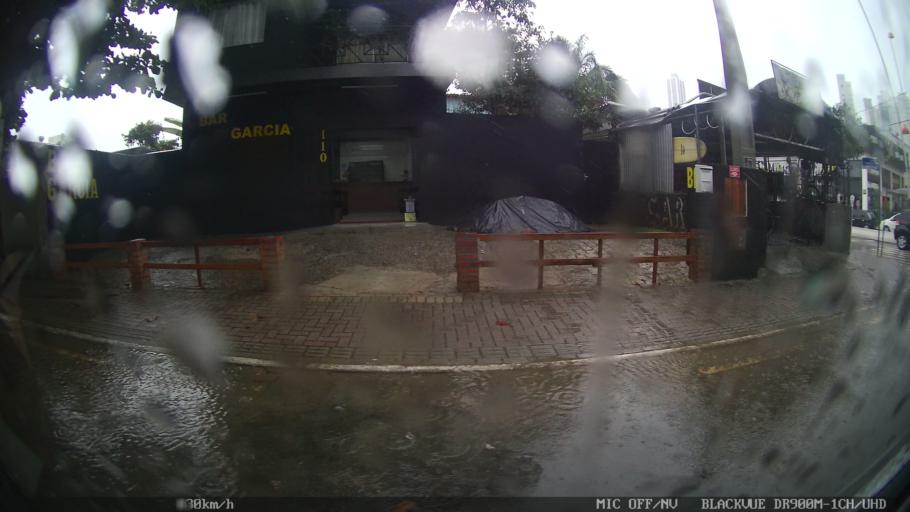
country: BR
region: Santa Catarina
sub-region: Balneario Camboriu
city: Balneario Camboriu
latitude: -27.0073
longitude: -48.6235
